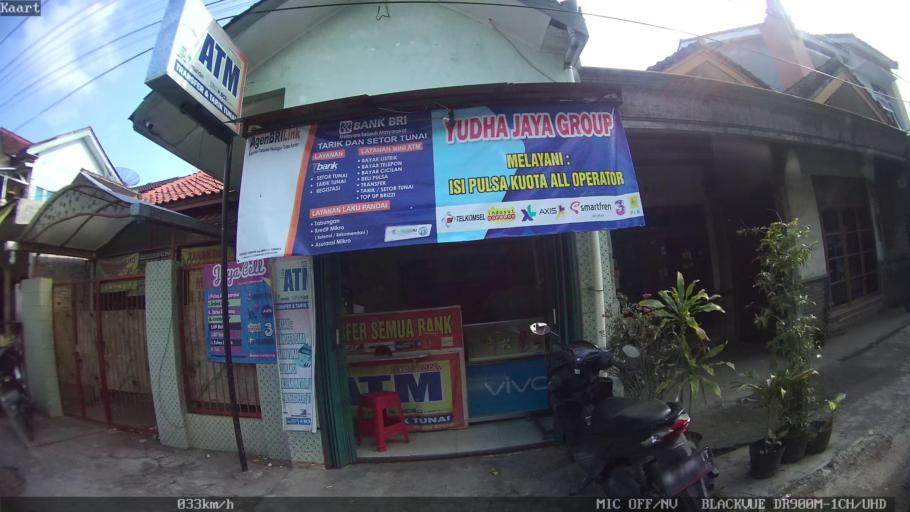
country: ID
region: Lampung
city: Kedaton
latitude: -5.4009
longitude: 105.2587
